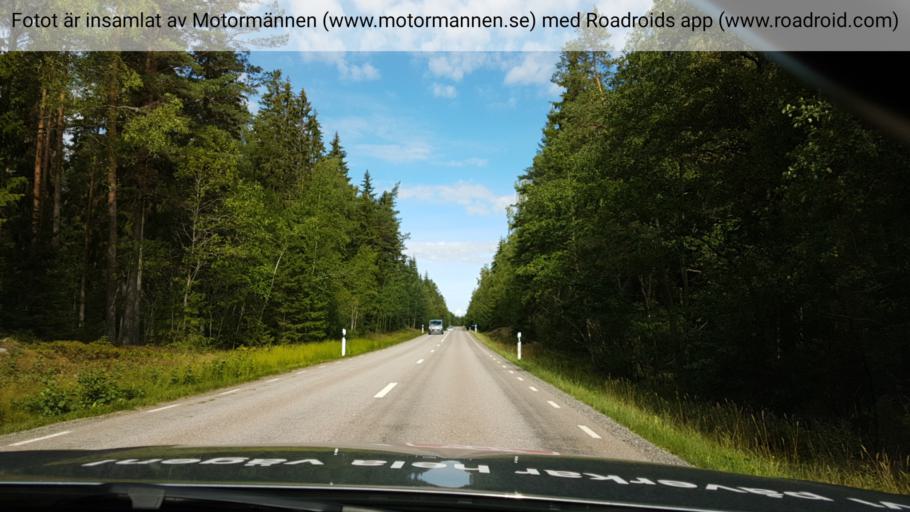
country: SE
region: Uppsala
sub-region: Heby Kommun
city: OEstervala
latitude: 60.0015
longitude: 17.3050
